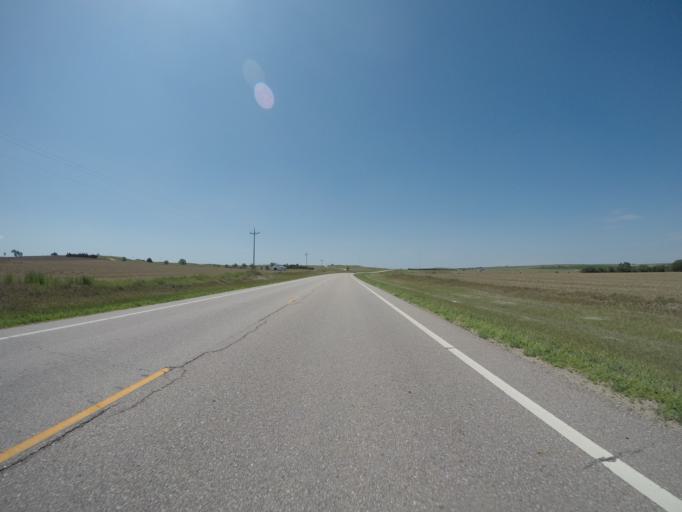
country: US
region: Kansas
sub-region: Osborne County
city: Osborne
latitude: 39.5018
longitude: -98.6935
